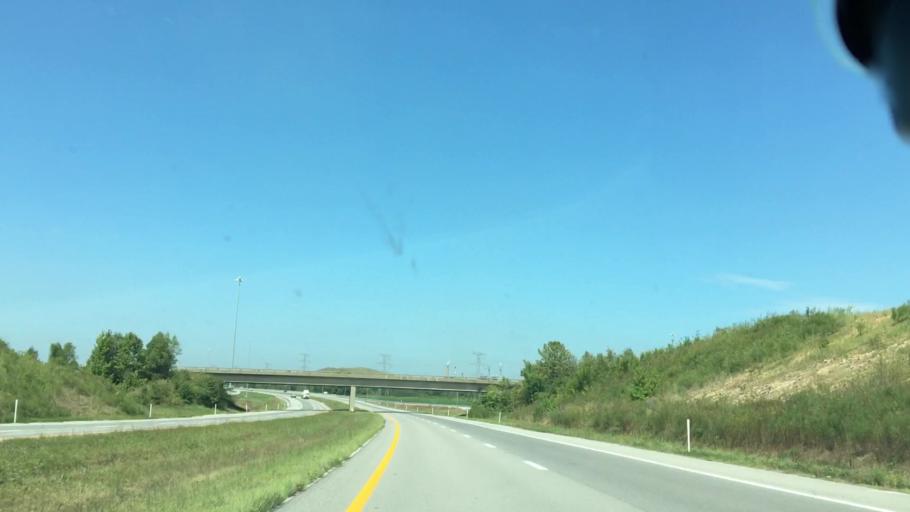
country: US
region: Kentucky
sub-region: Webster County
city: Sebree
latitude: 37.6084
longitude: -87.4975
